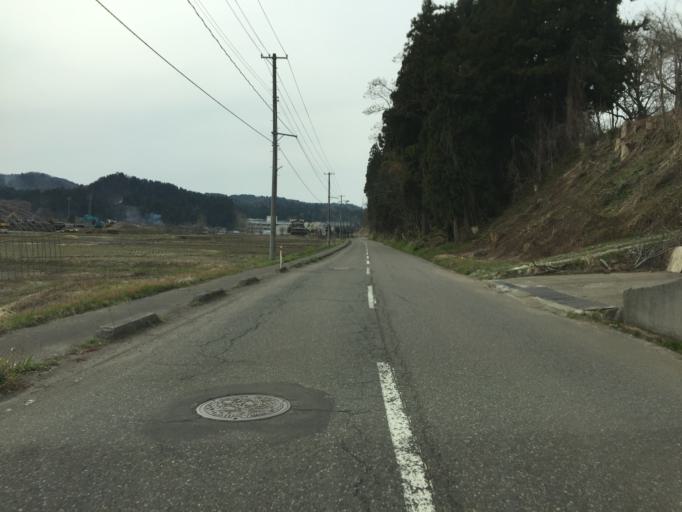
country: JP
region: Niigata
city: Tochio-honcho
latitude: 37.4455
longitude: 139.0242
